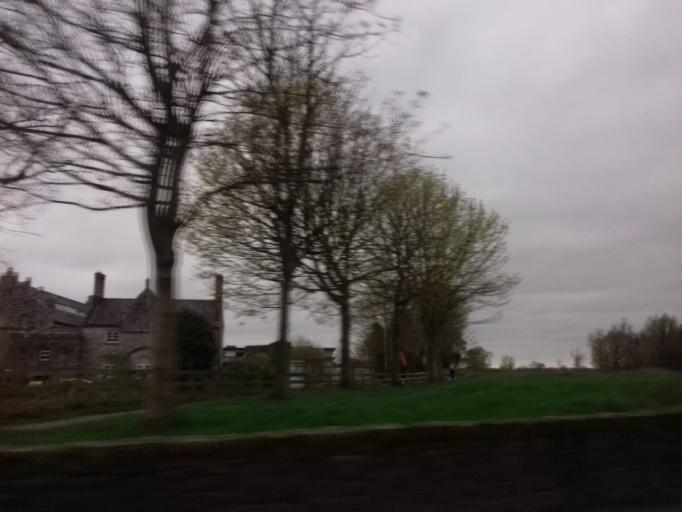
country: IE
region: Munster
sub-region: County Limerick
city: Adare
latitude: 52.5681
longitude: -8.7837
